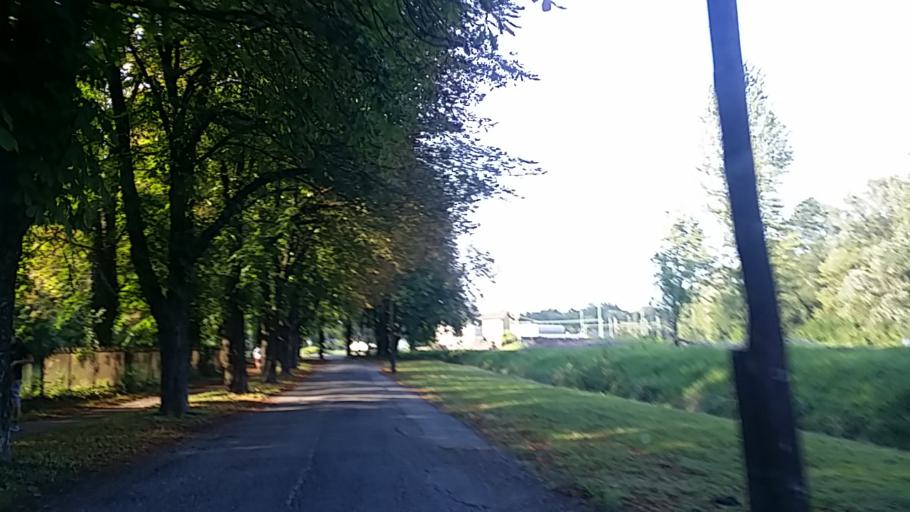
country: HU
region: Zala
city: Keszthely
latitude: 46.7549
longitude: 17.2457
